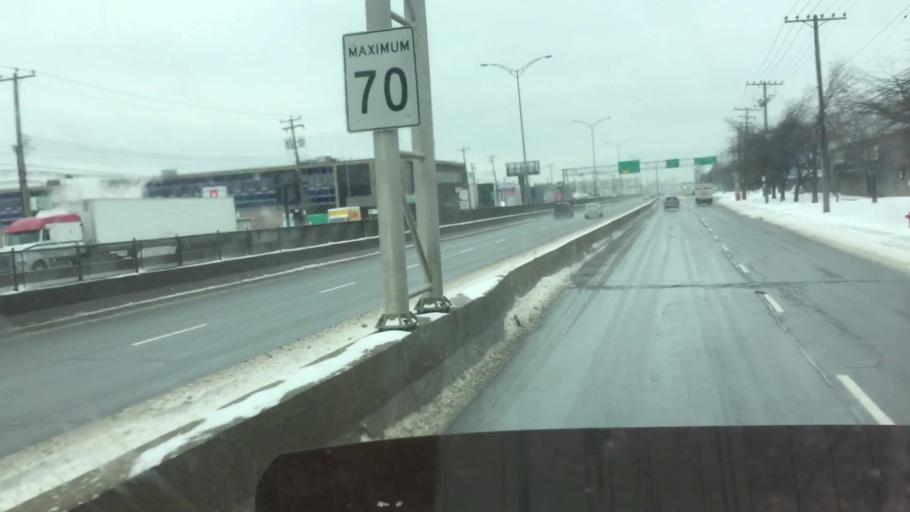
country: CA
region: Quebec
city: Dorval
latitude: 45.4683
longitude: -73.7151
